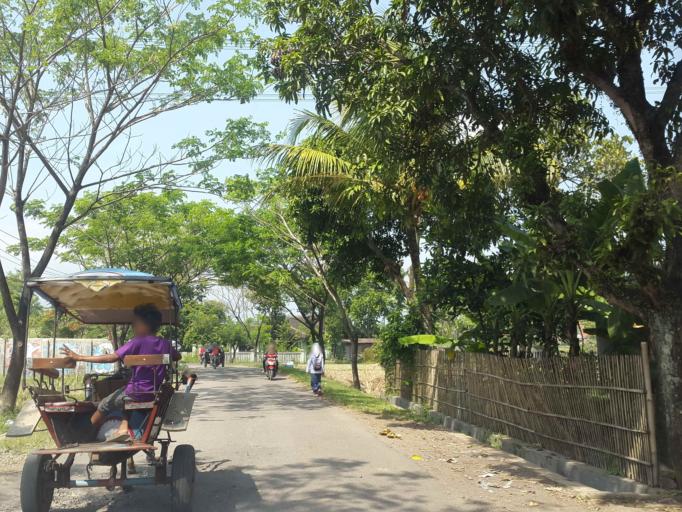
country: ID
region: West Java
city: Ciranjang-hilir
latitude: -6.8232
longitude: 107.2469
